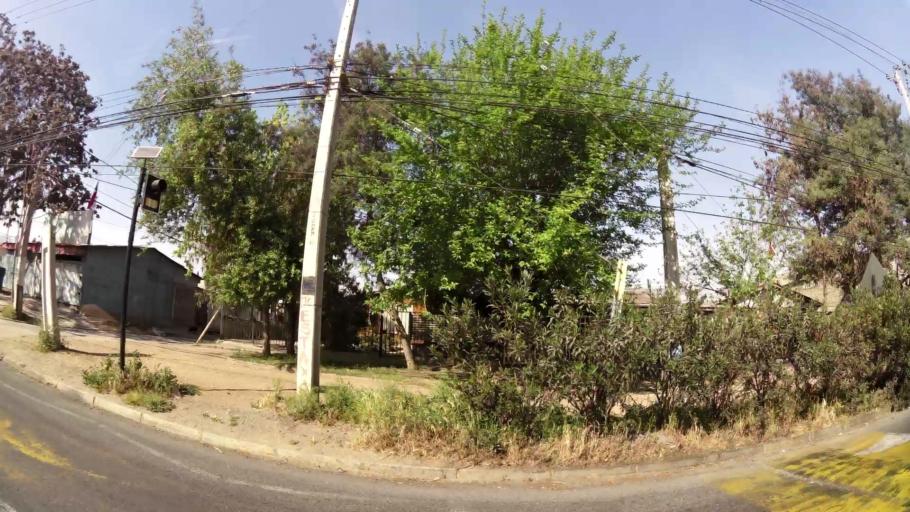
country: CL
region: Santiago Metropolitan
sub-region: Provincia de Santiago
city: Villa Presidente Frei, Nunoa, Santiago, Chile
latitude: -33.5007
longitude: -70.5847
